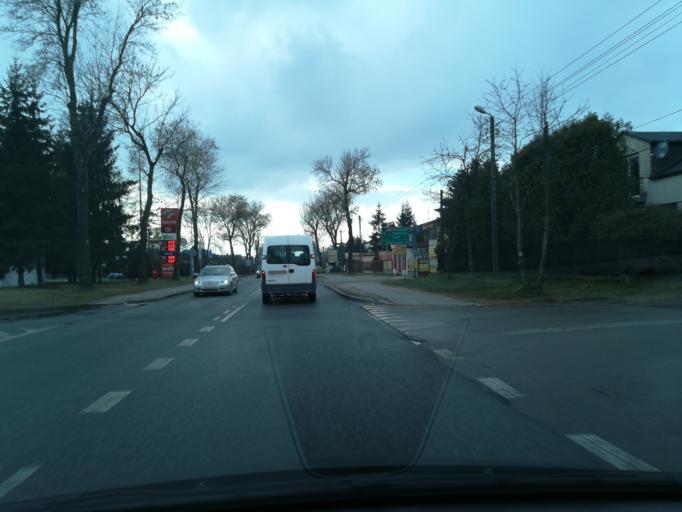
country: PL
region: Lodz Voivodeship
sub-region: Powiat radomszczanski
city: Radomsko
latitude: 51.0725
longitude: 19.4198
